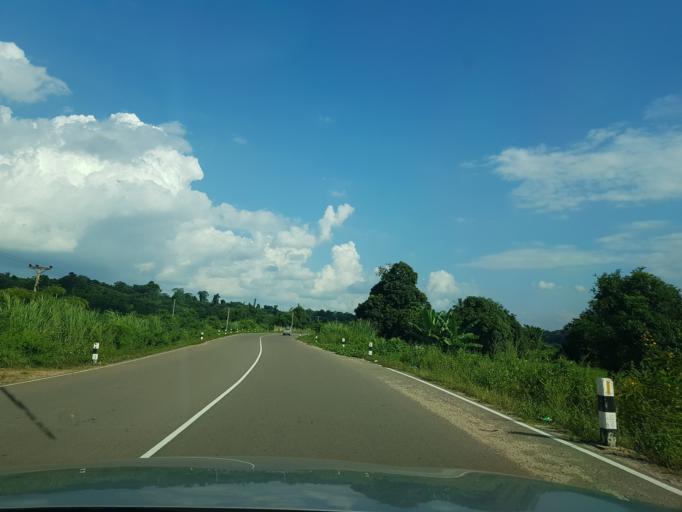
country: TH
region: Nong Khai
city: Pho Tak
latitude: 17.9943
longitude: 102.4185
